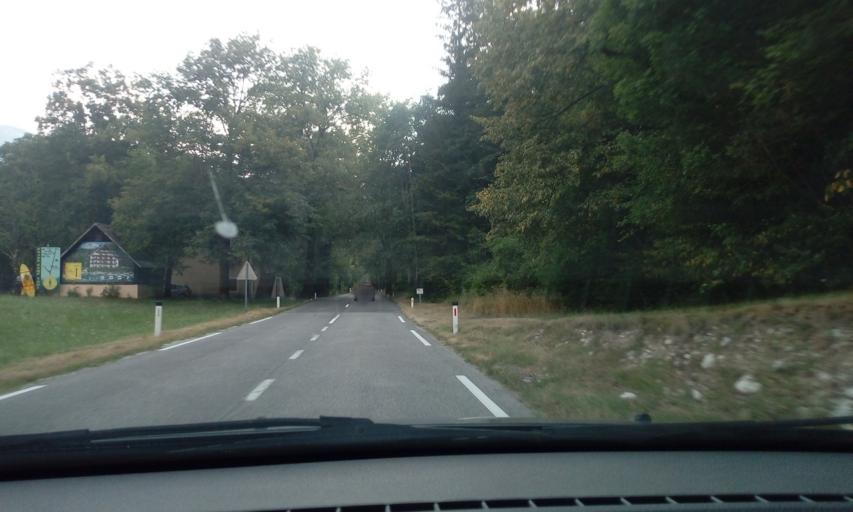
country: SI
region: Bovec
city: Bovec
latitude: 46.3544
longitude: 13.5844
